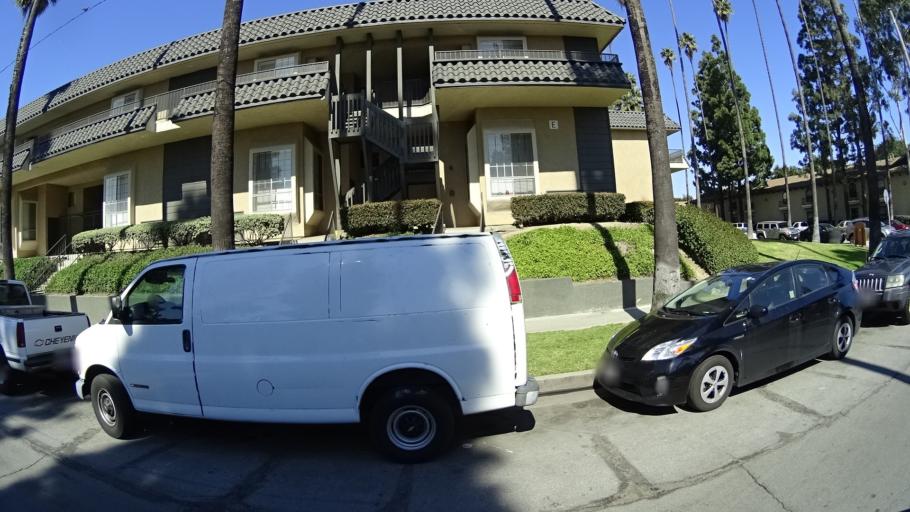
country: US
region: California
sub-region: Orange County
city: Anaheim
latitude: 33.8161
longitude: -117.9397
